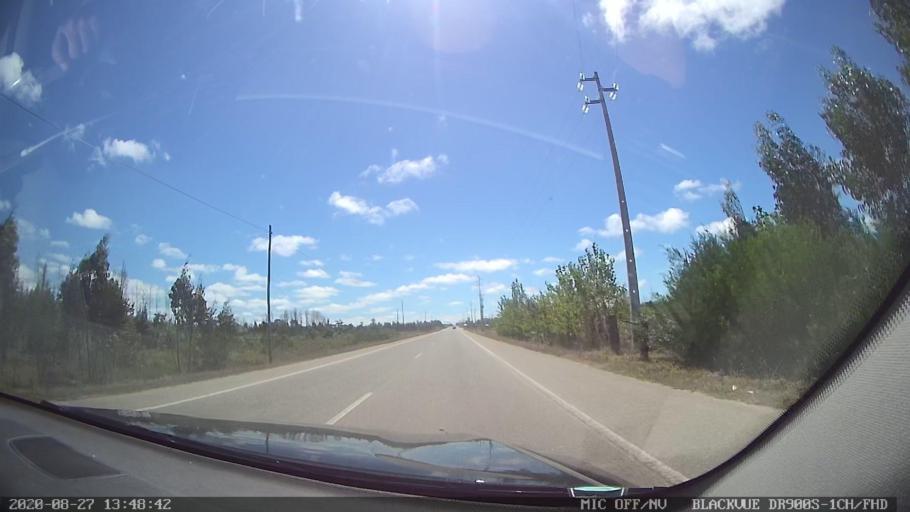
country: PT
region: Coimbra
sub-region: Mira
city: Mira
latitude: 40.3747
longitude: -8.7453
